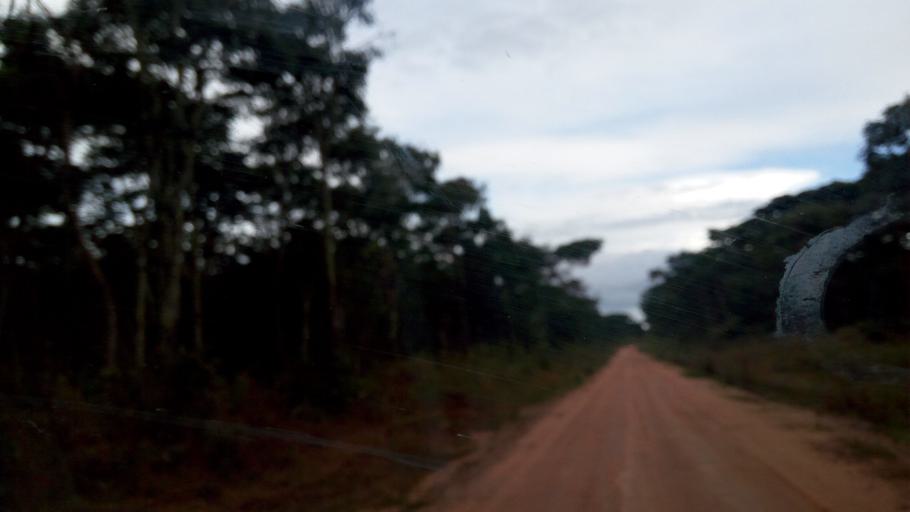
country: CD
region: Katanga
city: Kalemie
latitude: -6.6580
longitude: 29.0680
